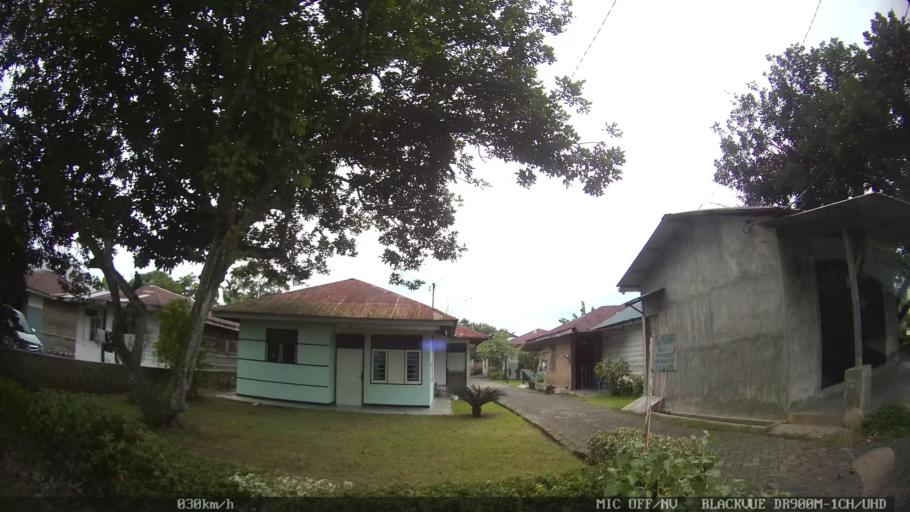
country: ID
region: North Sumatra
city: Sunggal
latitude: 3.6247
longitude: 98.5904
